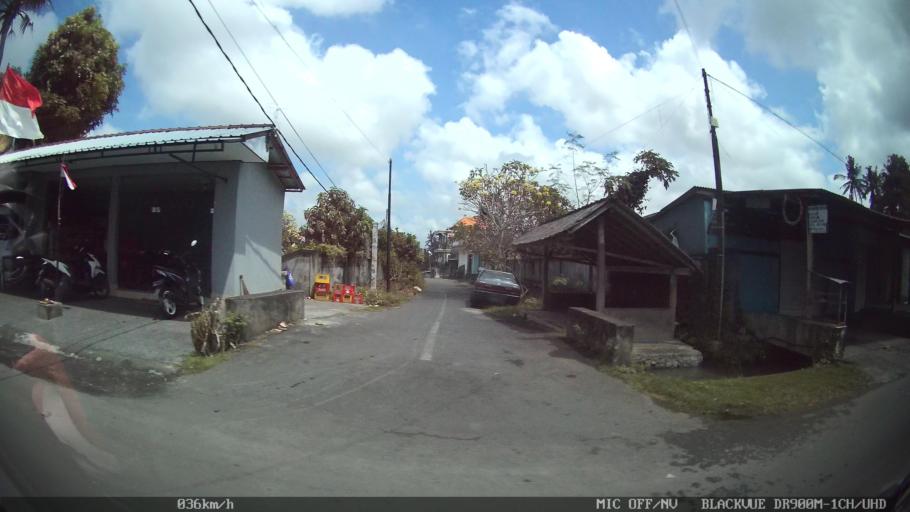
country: ID
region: Bali
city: Banjar Desa
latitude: -8.5746
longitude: 115.2867
